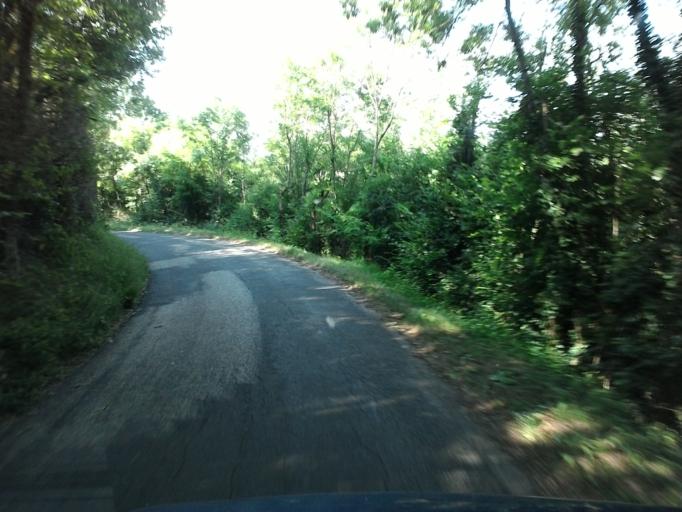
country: FR
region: Rhone-Alpes
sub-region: Departement de l'Ain
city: Sault-Brenaz
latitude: 45.8601
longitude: 5.4098
